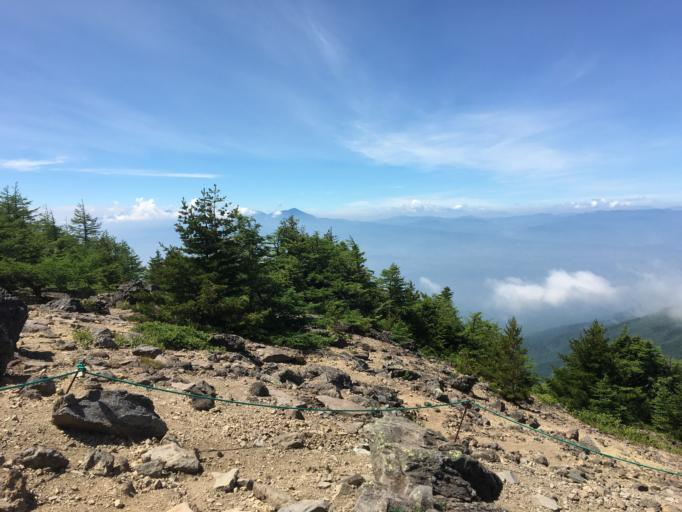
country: JP
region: Nagano
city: Komoro
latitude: 36.4027
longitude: 138.4793
